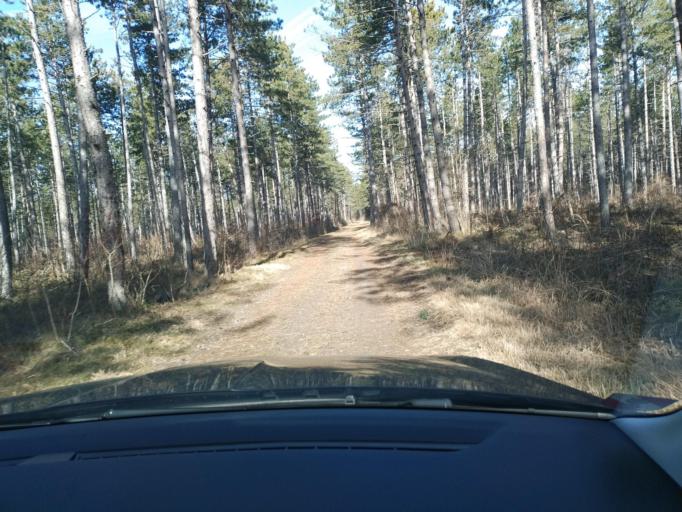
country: AT
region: Lower Austria
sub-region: Politischer Bezirk Neunkirchen
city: Breitenau
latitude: 47.7464
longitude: 16.1635
